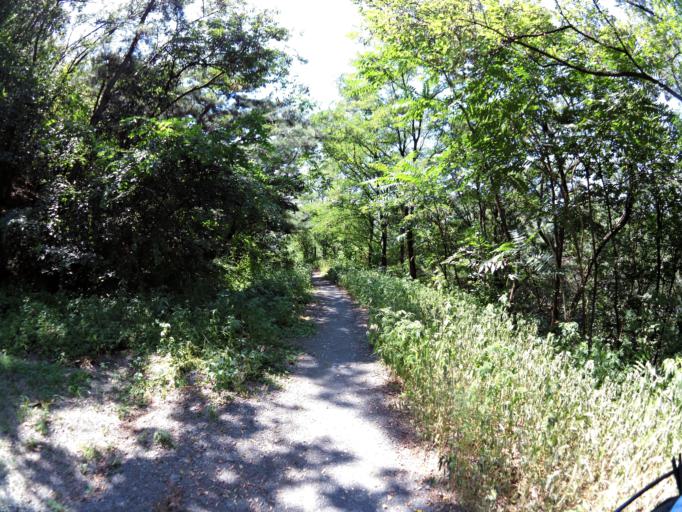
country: KR
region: Daegu
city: Daegu
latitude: 35.8513
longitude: 128.6465
